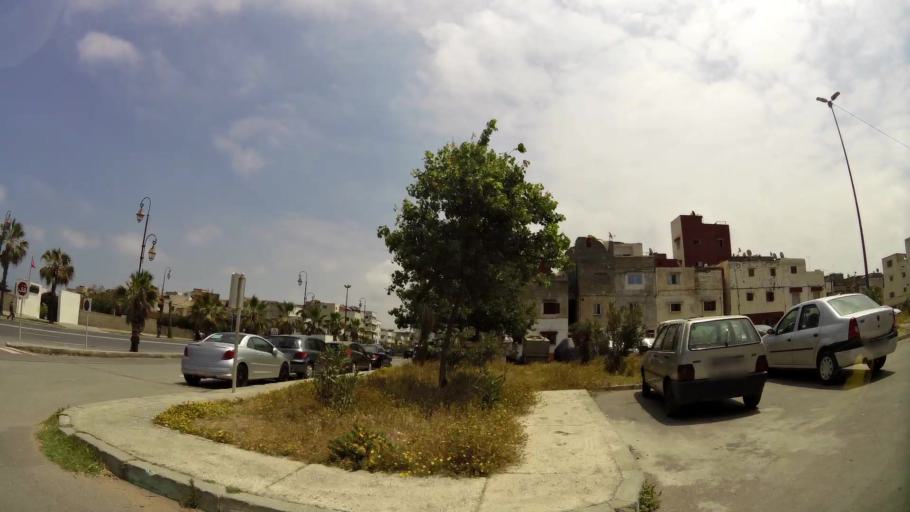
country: MA
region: Rabat-Sale-Zemmour-Zaer
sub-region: Rabat
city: Rabat
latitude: 33.9901
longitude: -6.8788
